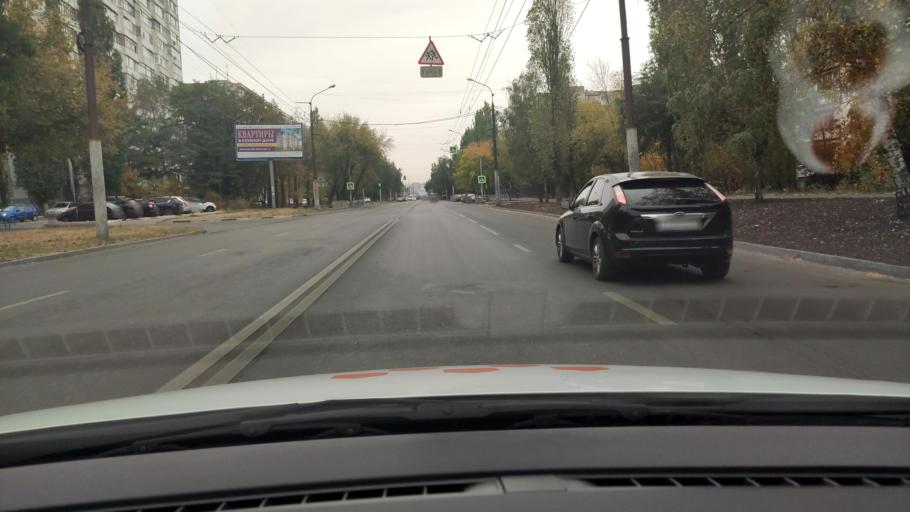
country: RU
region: Voronezj
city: Voronezh
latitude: 51.7033
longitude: 39.1746
